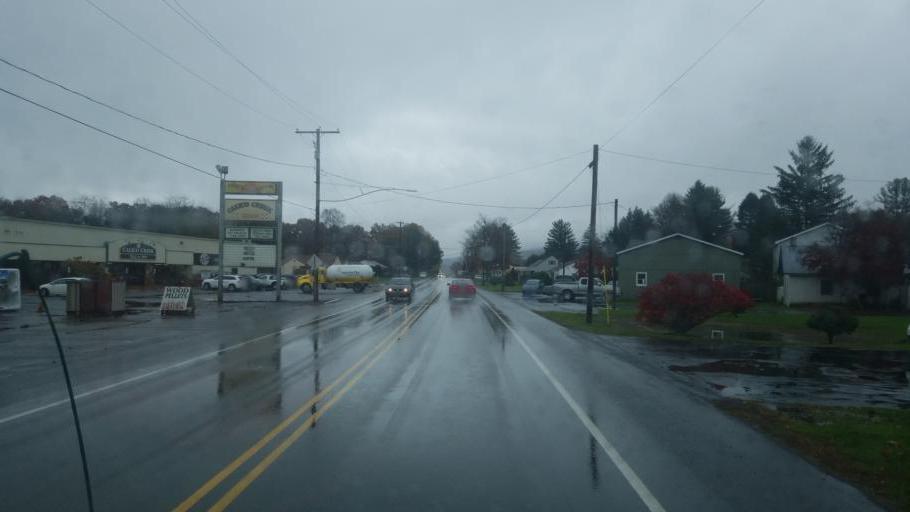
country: US
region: Pennsylvania
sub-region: Clinton County
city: Mill Hall
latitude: 41.1123
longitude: -77.4974
